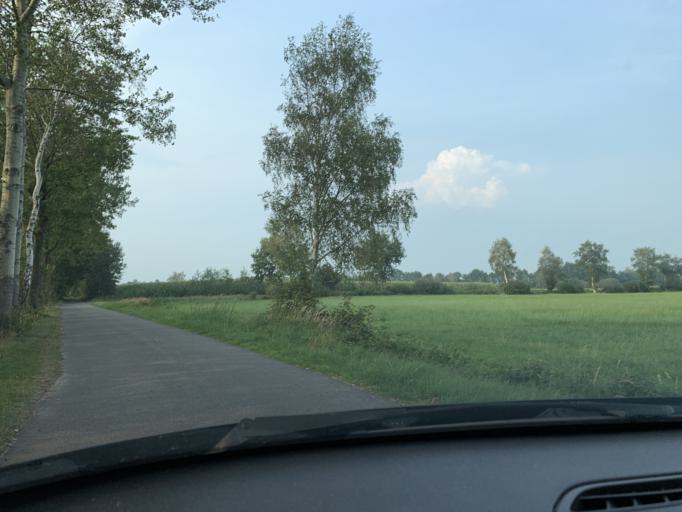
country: DE
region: Lower Saxony
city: Apen
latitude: 53.2370
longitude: 7.8193
